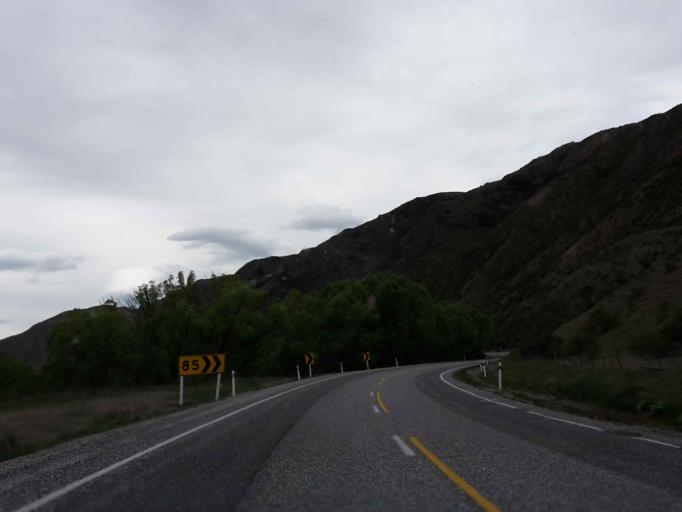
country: NZ
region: Otago
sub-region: Queenstown-Lakes District
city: Wanaka
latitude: -44.6310
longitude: 169.5165
